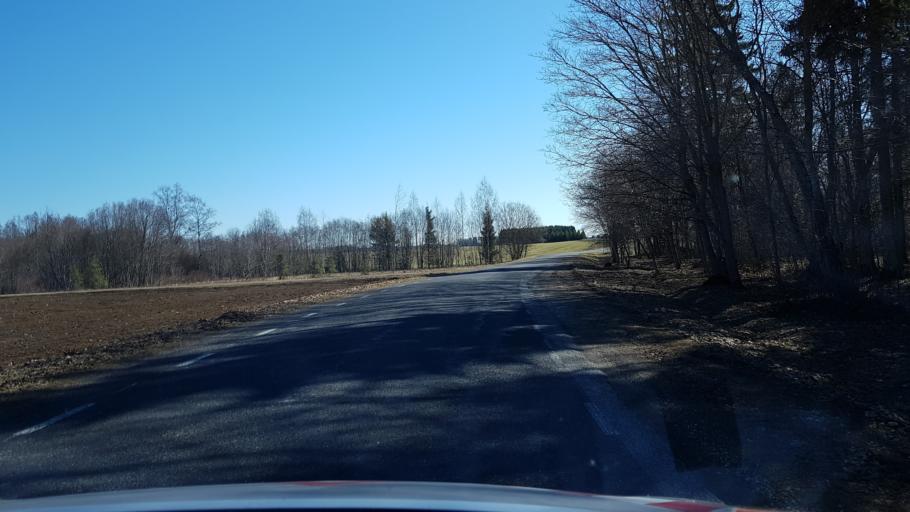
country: EE
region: Laeaene-Virumaa
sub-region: Kadrina vald
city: Kadrina
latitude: 59.4415
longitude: 26.1507
